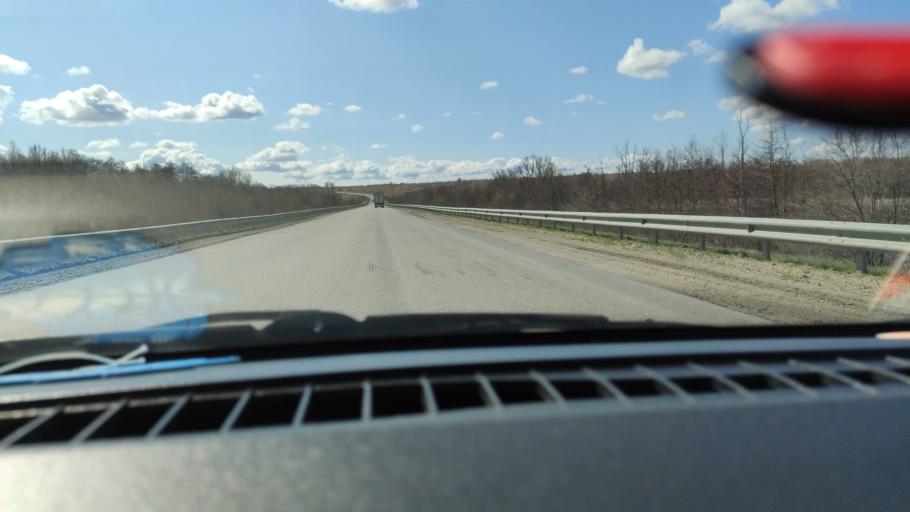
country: RU
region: Samara
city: Varlamovo
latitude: 53.1319
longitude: 48.2876
